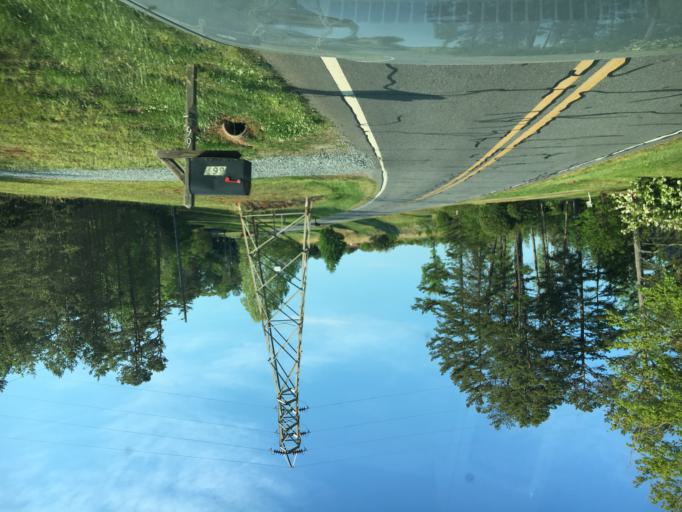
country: US
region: North Carolina
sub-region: Rutherford County
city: Rutherfordton
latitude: 35.3406
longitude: -81.9863
